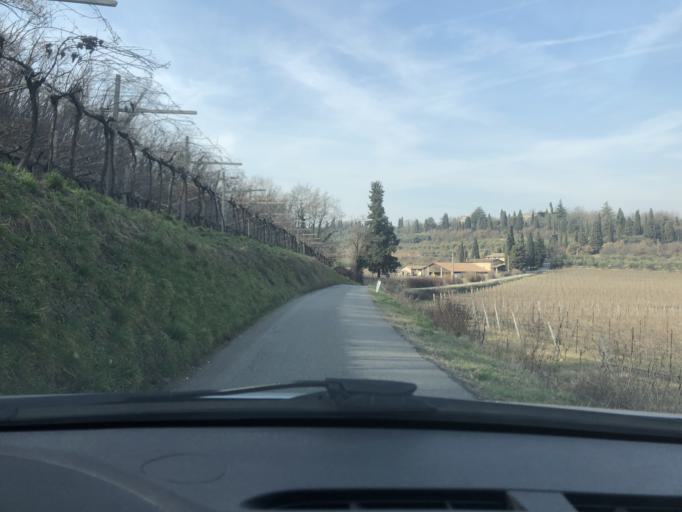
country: IT
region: Veneto
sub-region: Provincia di Verona
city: Costermano
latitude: 45.5679
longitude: 10.7347
